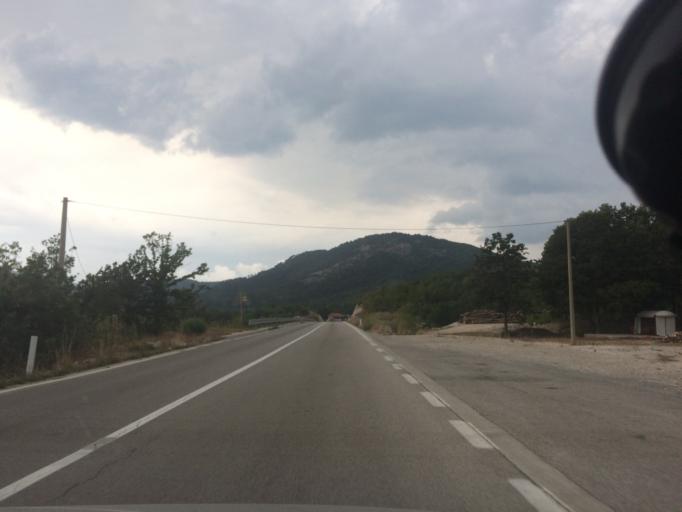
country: ME
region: Kotor
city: Risan
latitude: 42.6681
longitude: 18.6564
